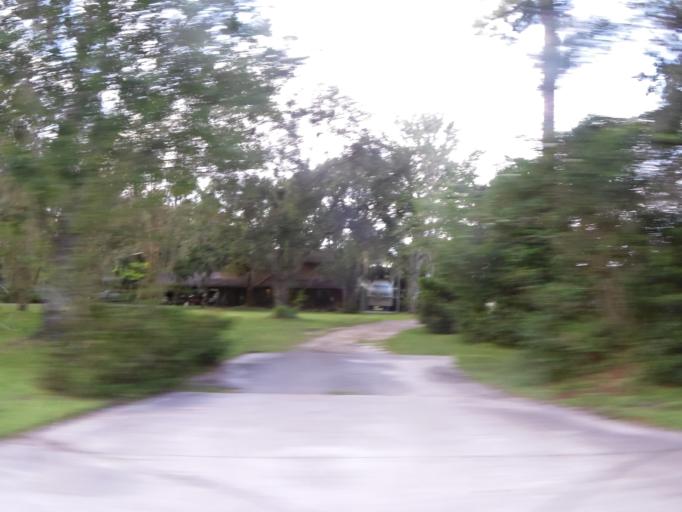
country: US
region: Florida
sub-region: Saint Johns County
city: Fruit Cove
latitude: 30.1410
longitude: -81.6169
